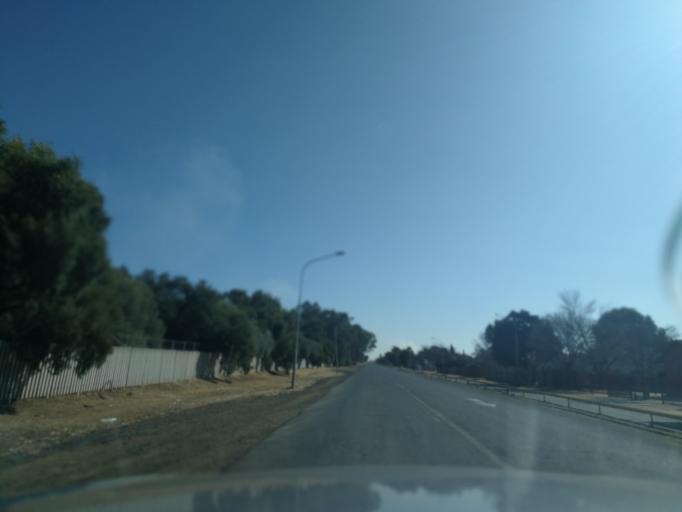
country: ZA
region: Orange Free State
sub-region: Fezile Dabi District Municipality
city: Kroonstad
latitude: -27.6421
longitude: 27.2211
